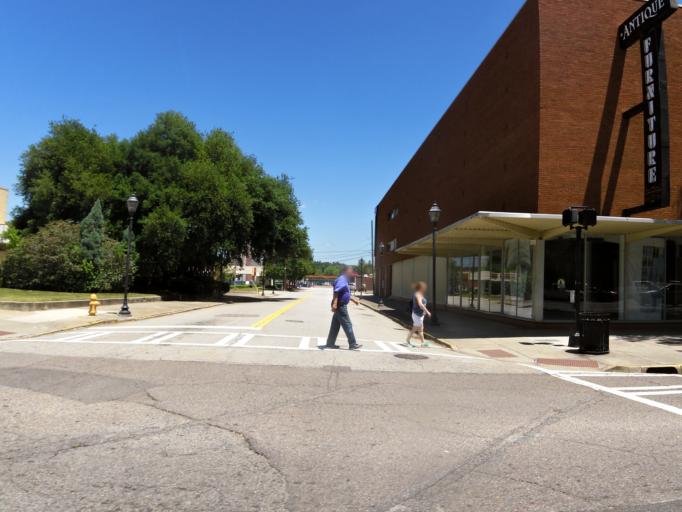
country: US
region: Georgia
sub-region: Richmond County
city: Augusta
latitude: 33.4773
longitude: -81.9710
